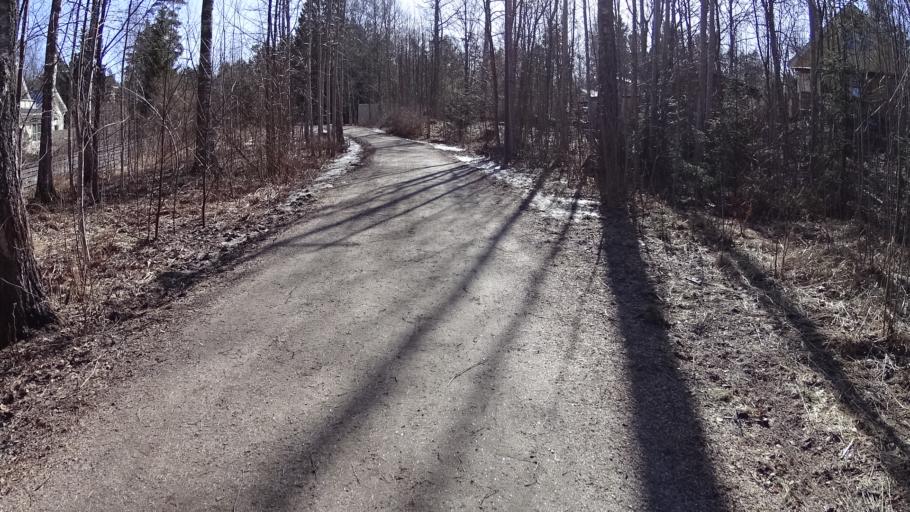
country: FI
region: Uusimaa
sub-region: Helsinki
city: Kilo
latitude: 60.1973
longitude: 24.7988
